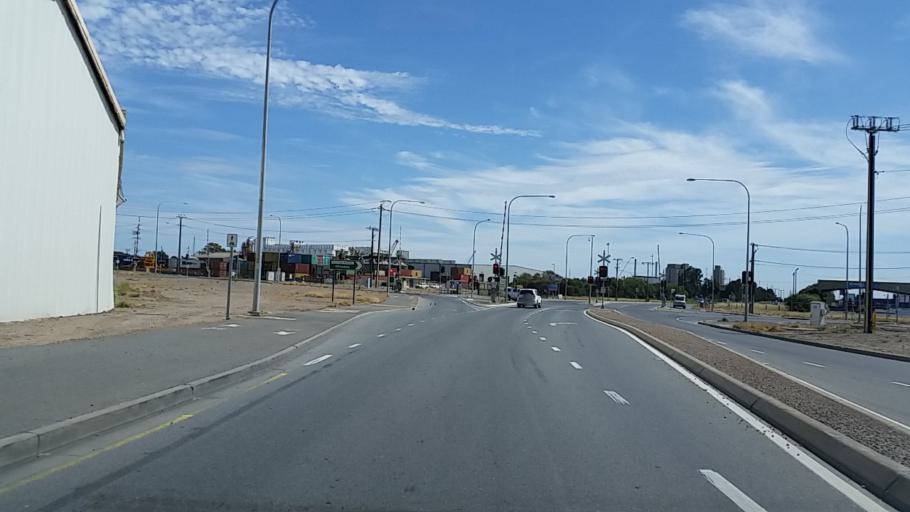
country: AU
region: South Australia
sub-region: Port Adelaide Enfield
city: Birkenhead
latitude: -34.8369
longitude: 138.5147
